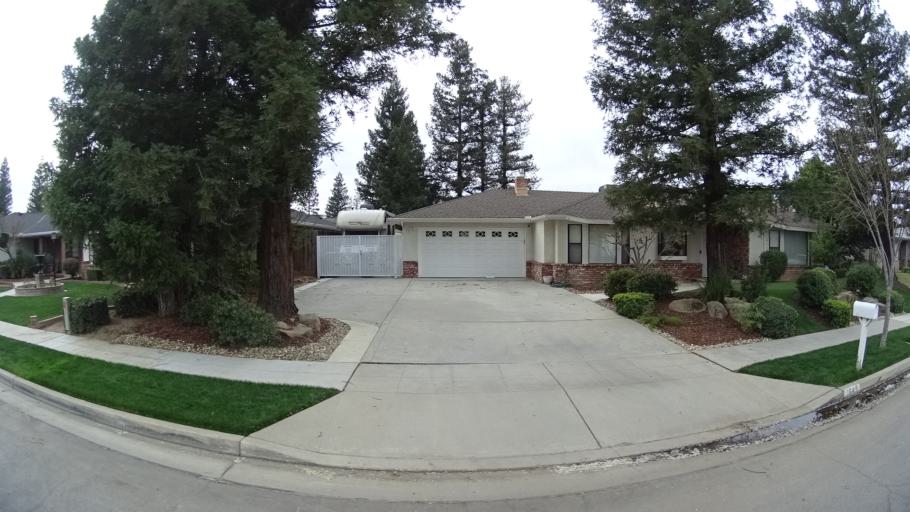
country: US
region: California
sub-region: Fresno County
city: Clovis
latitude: 36.8484
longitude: -119.7537
